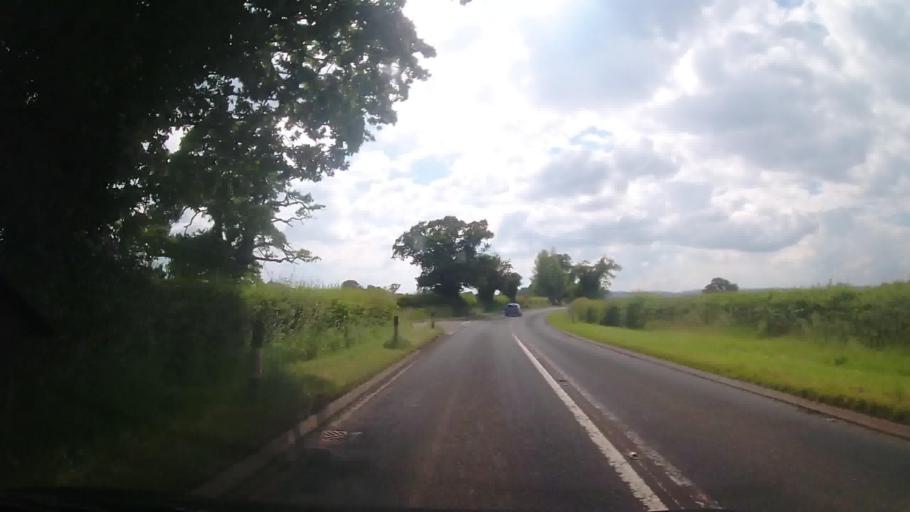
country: GB
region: England
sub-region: Shropshire
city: Whittington
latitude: 52.8849
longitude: -2.9704
